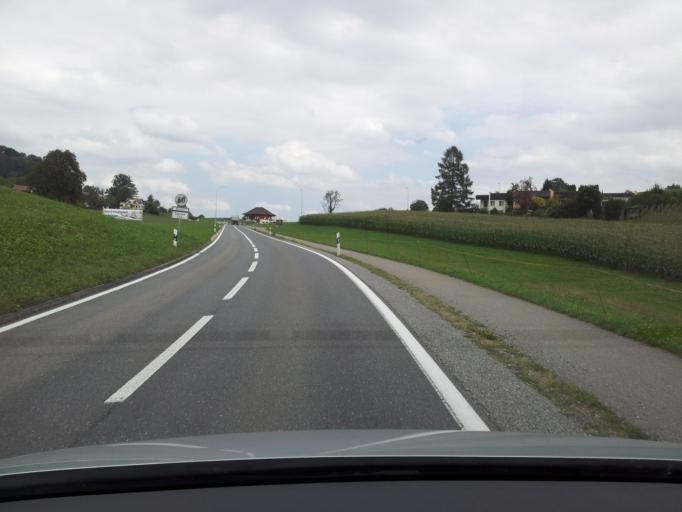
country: CH
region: Lucerne
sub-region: Sursee District
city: Buttisholz
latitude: 47.1181
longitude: 8.1034
